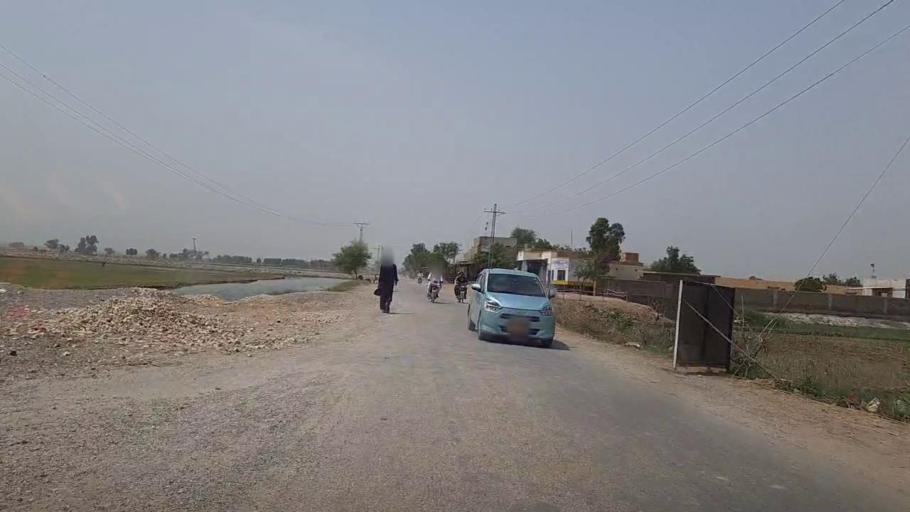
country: PK
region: Sindh
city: Radhan
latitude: 27.1687
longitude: 67.9459
